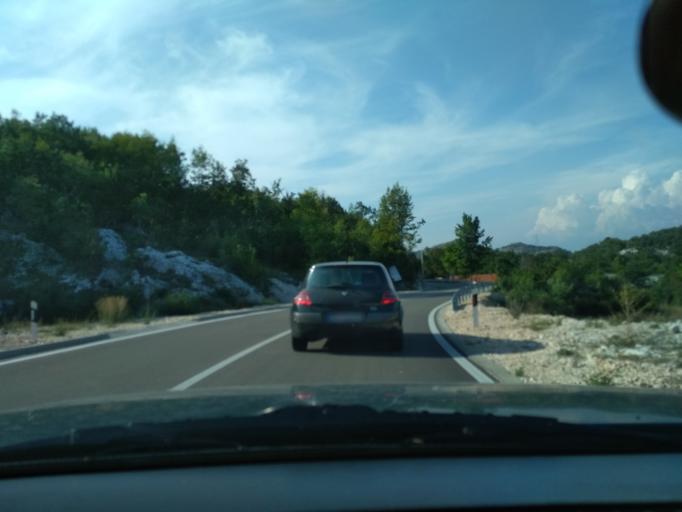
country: ME
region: Cetinje
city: Cetinje
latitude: 42.4153
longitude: 18.8801
